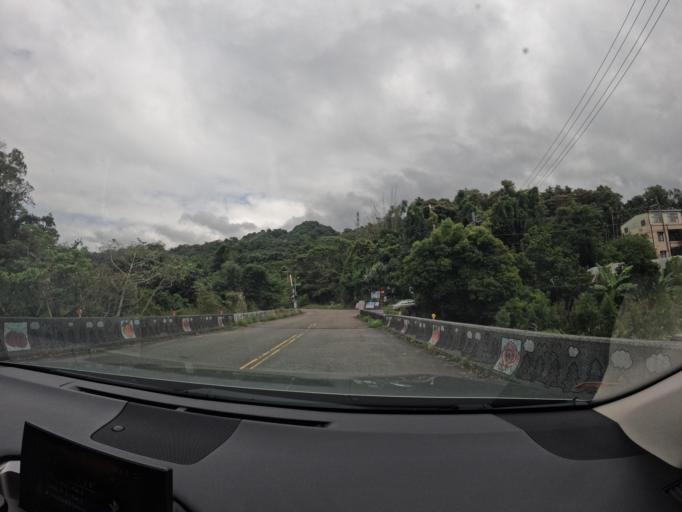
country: TW
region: Taiwan
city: Fengyuan
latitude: 24.3156
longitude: 120.8795
